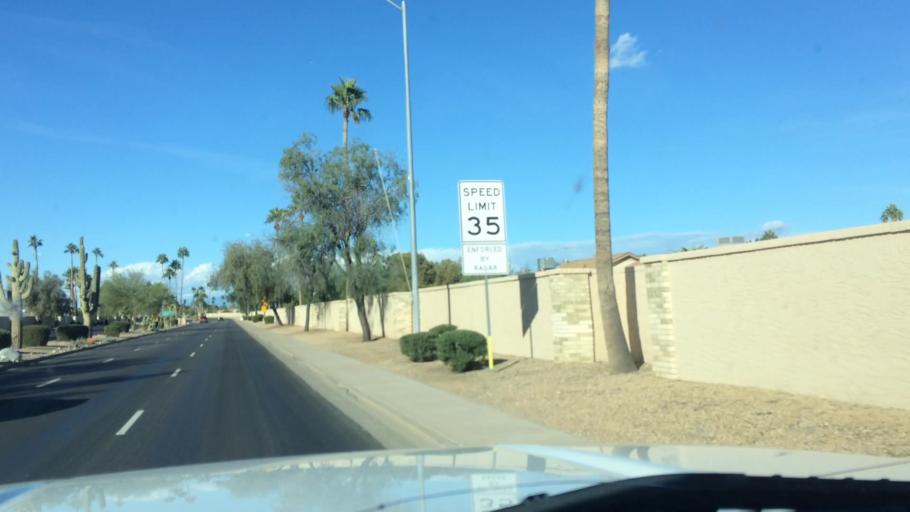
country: US
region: Arizona
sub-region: Maricopa County
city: Surprise
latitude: 33.6399
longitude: -112.3344
